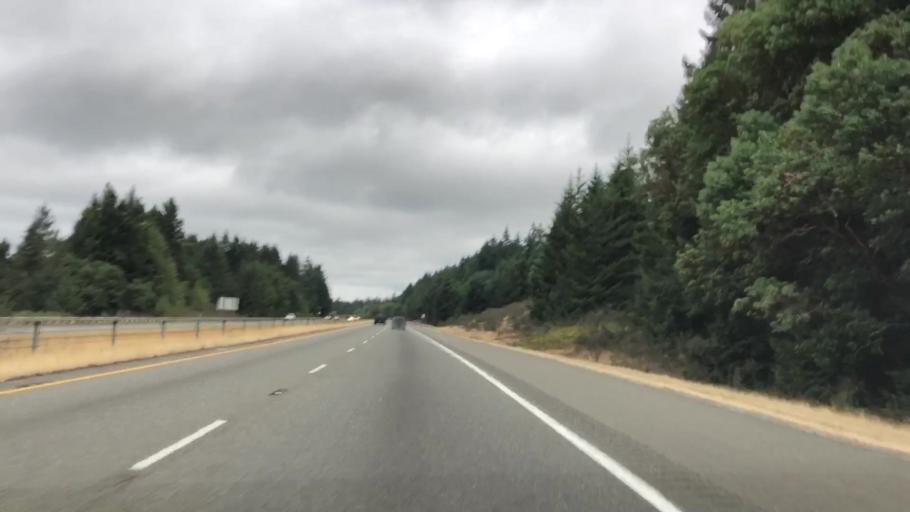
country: US
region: Washington
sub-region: Pierce County
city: Purdy
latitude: 47.3799
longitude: -122.6155
